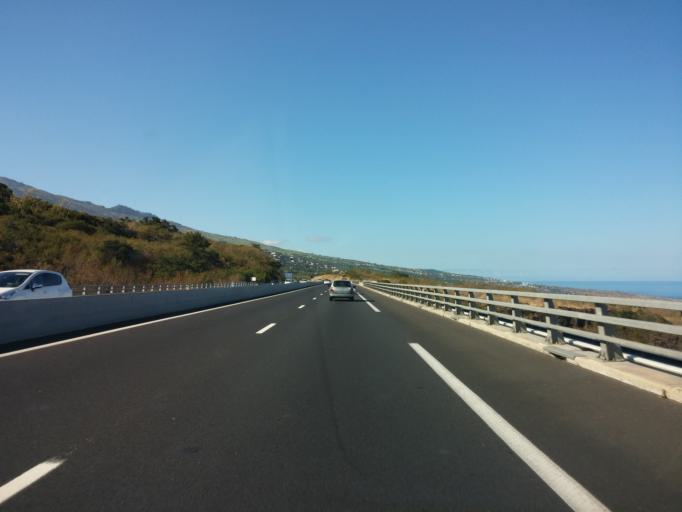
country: RE
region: Reunion
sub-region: Reunion
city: Saint-Leu
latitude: -21.1489
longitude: 55.2897
